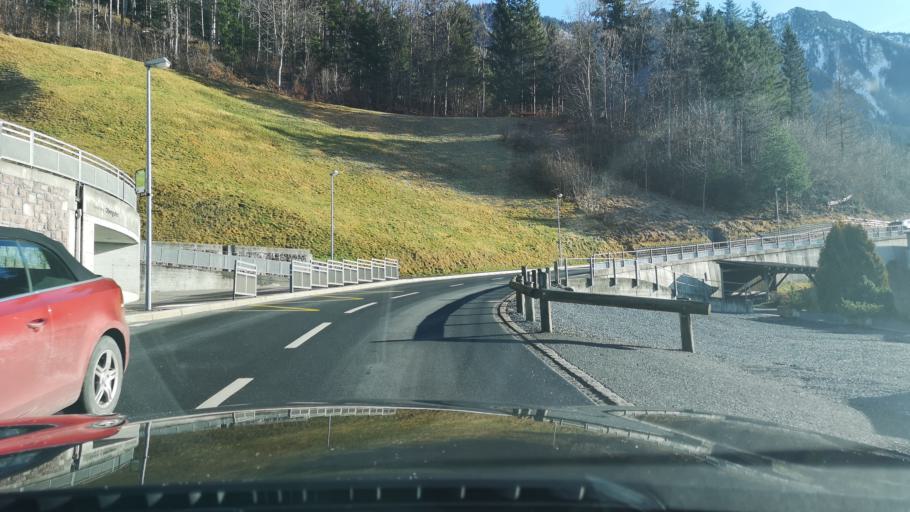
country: LI
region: Triesenberg
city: Triesenberg
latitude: 47.1168
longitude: 9.5471
